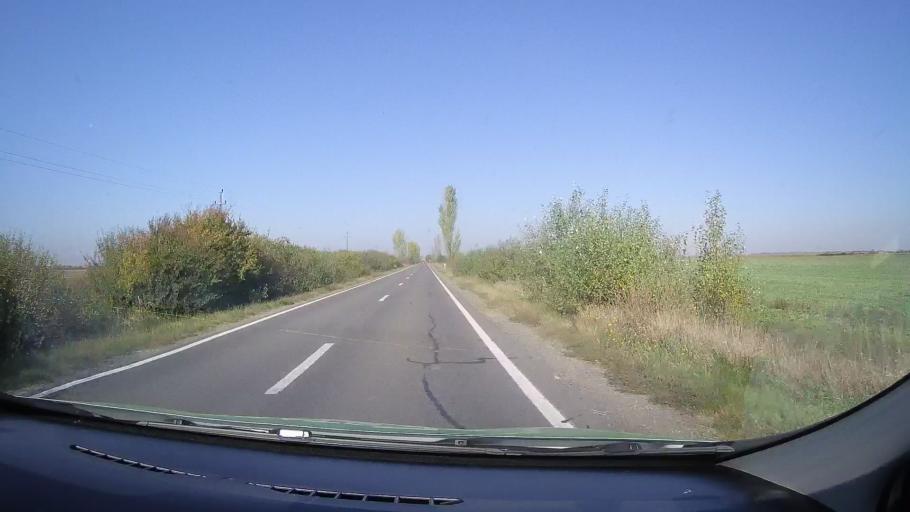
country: RO
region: Satu Mare
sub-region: Comuna Urziceni
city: Urziceni
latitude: 47.7087
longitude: 22.4296
